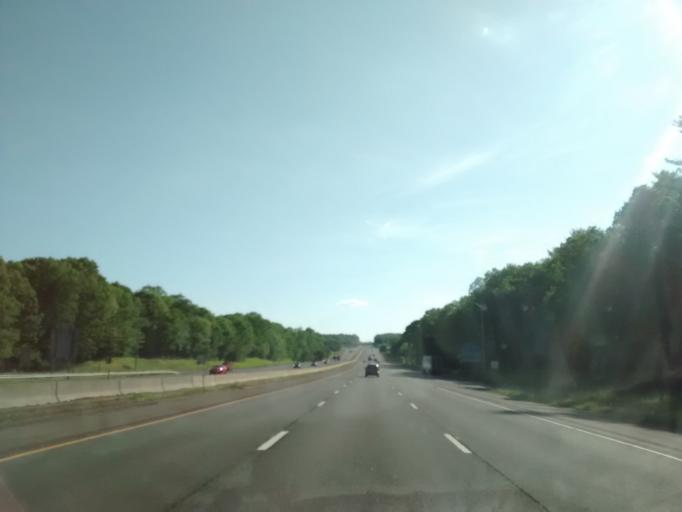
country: US
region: Connecticut
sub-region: Tolland County
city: Stafford Springs
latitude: 41.8925
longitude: -72.2985
